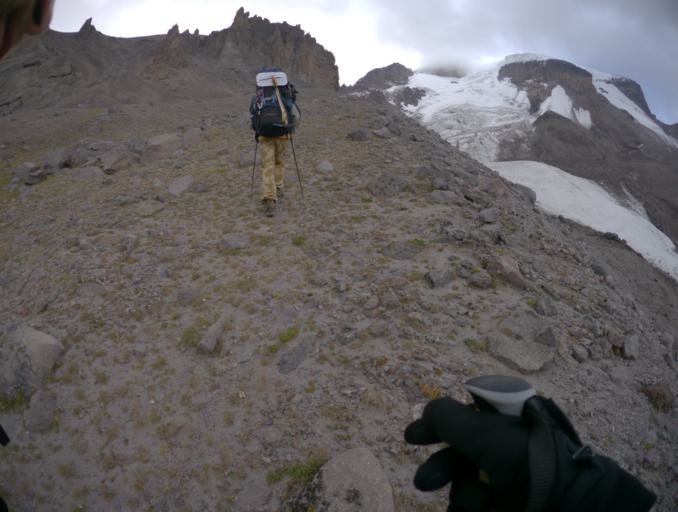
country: RU
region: Kabardino-Balkariya
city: Terskol
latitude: 43.3817
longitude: 42.3927
